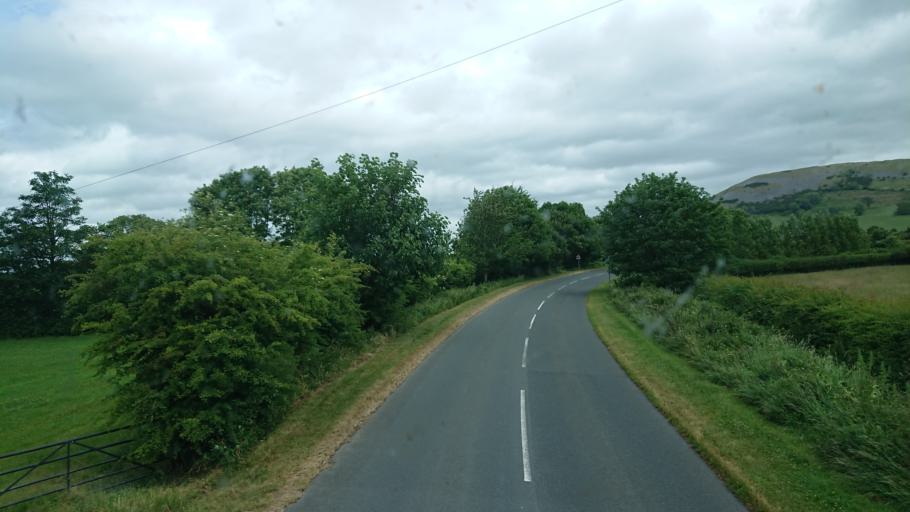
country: GB
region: England
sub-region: Cumbria
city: Milnthorpe
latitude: 54.2104
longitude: -2.7285
